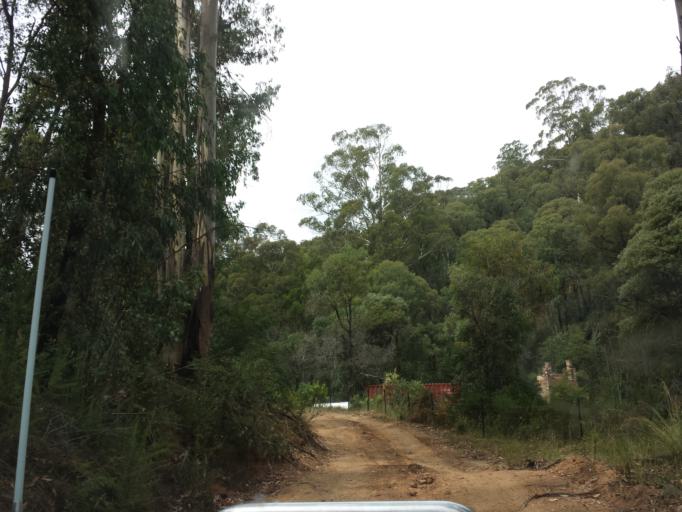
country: AU
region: Victoria
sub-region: Wellington
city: Heyfield
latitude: -37.7549
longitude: 146.5018
